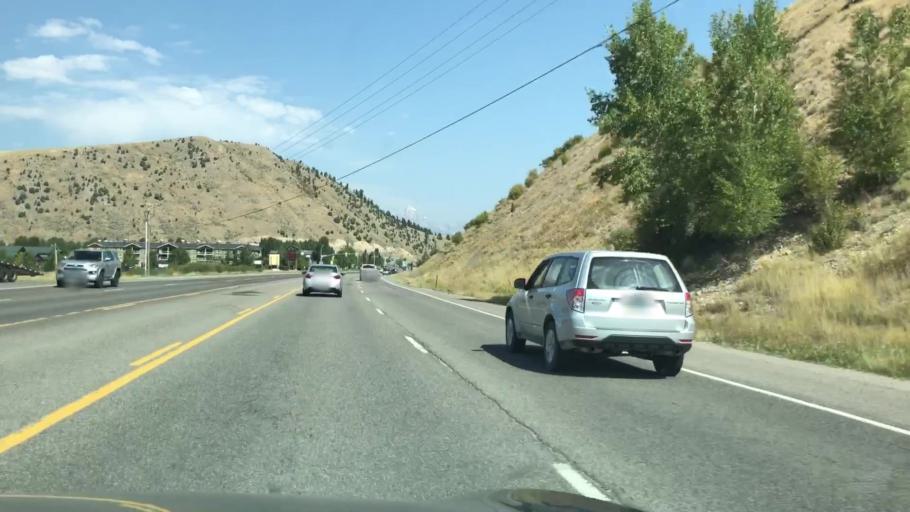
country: US
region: Wyoming
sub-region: Teton County
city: Rafter J Ranch
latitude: 43.4555
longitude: -110.7931
